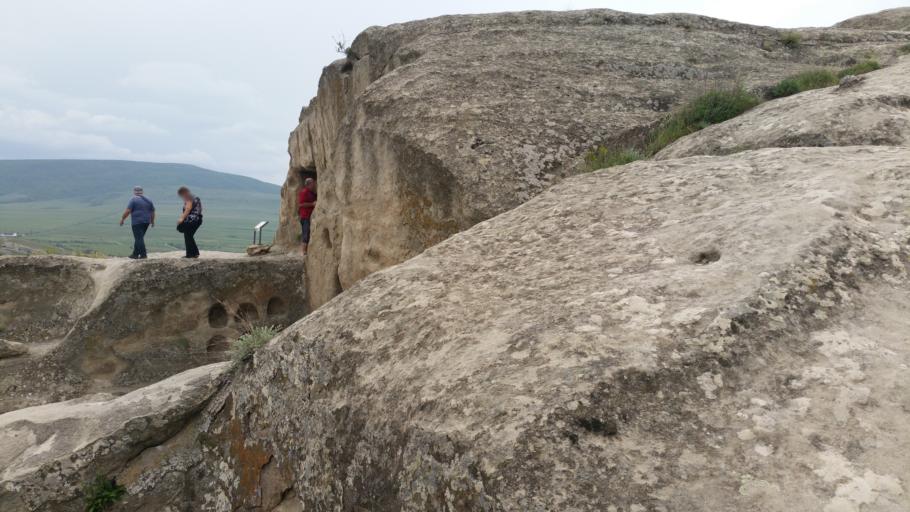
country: GE
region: Shida Kartli
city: Gori
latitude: 41.9676
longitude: 44.2071
